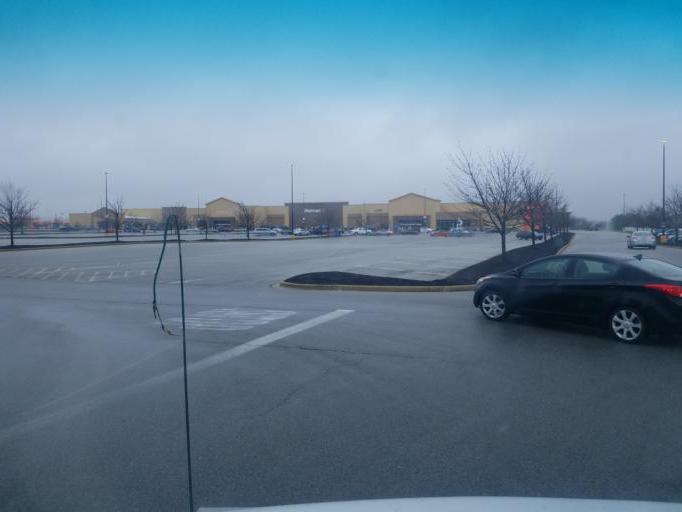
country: US
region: Ohio
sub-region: Wood County
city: Bowling Green
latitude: 41.3561
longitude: -83.6536
